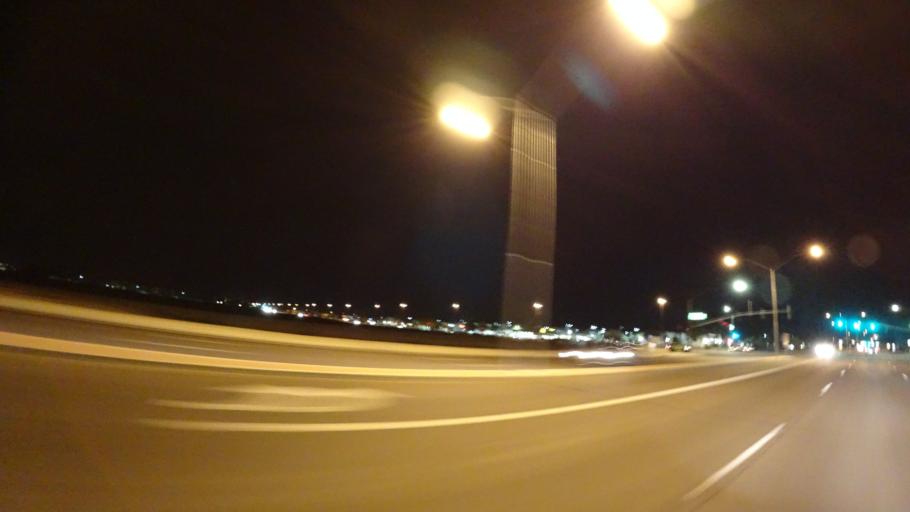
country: US
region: Arizona
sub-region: Maricopa County
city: Gilbert
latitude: 33.3793
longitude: -111.7214
